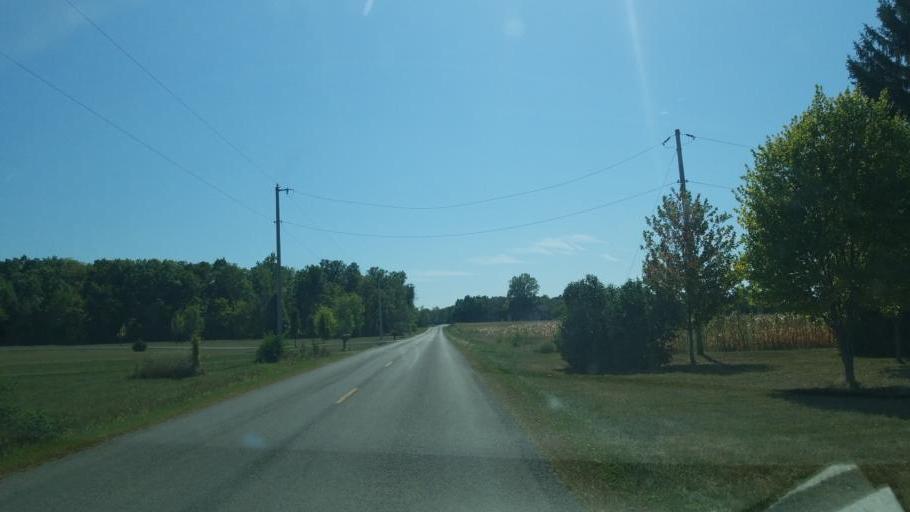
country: US
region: Ohio
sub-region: Logan County
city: Northwood
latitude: 40.4641
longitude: -83.7878
